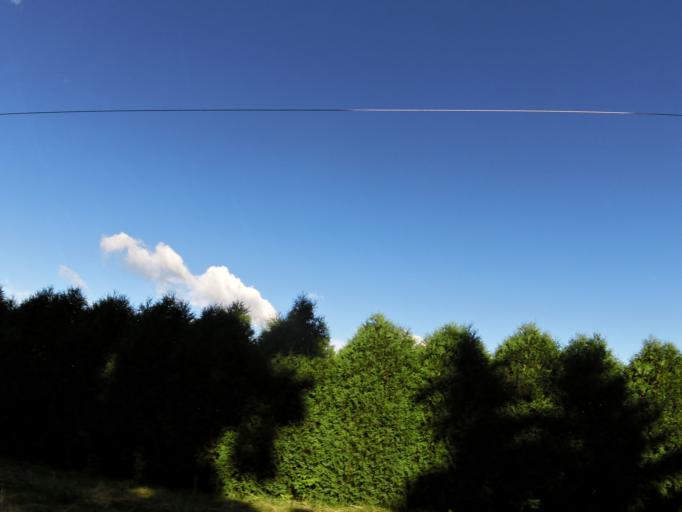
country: US
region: Minnesota
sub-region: Dakota County
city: Hastings
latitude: 44.8082
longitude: -92.8630
